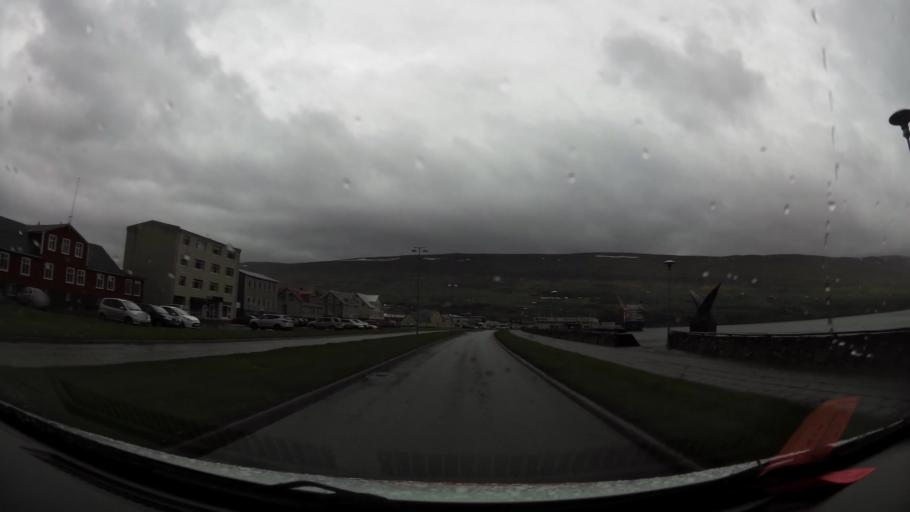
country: IS
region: Northeast
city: Akureyri
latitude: 65.6845
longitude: -18.0853
